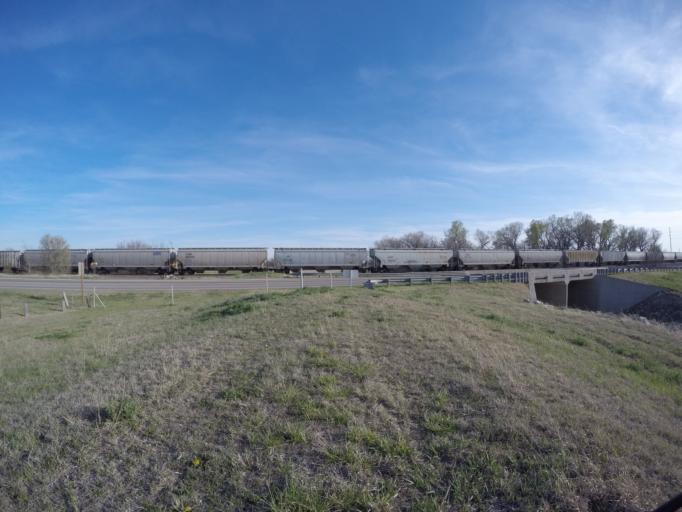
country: US
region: Kansas
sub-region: Saline County
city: Salina
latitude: 38.8440
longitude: -97.6306
